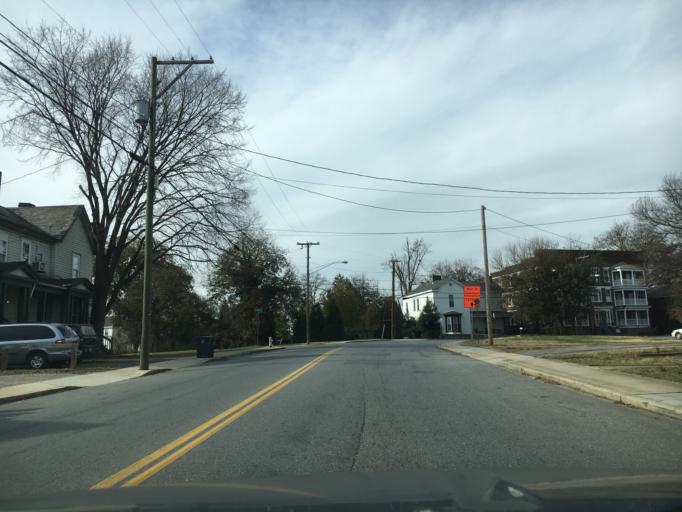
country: US
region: Virginia
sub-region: City of Lynchburg
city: Lynchburg
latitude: 37.4036
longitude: -79.1428
